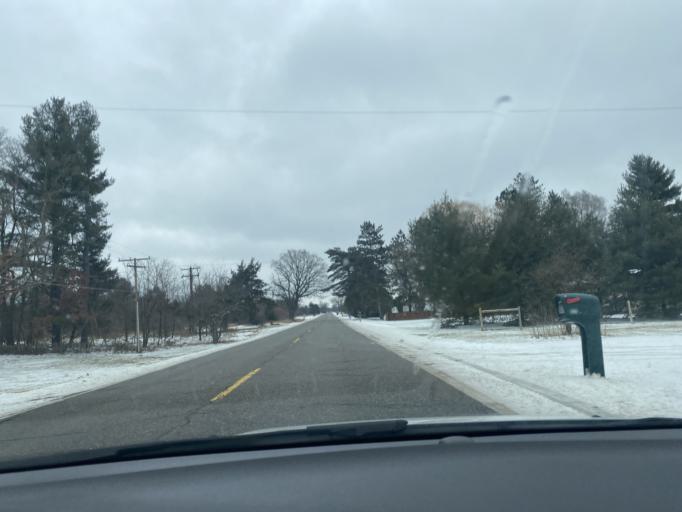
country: US
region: Michigan
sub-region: Lapeer County
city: Barnes Lake-Millers Lake
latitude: 43.2060
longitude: -83.2684
